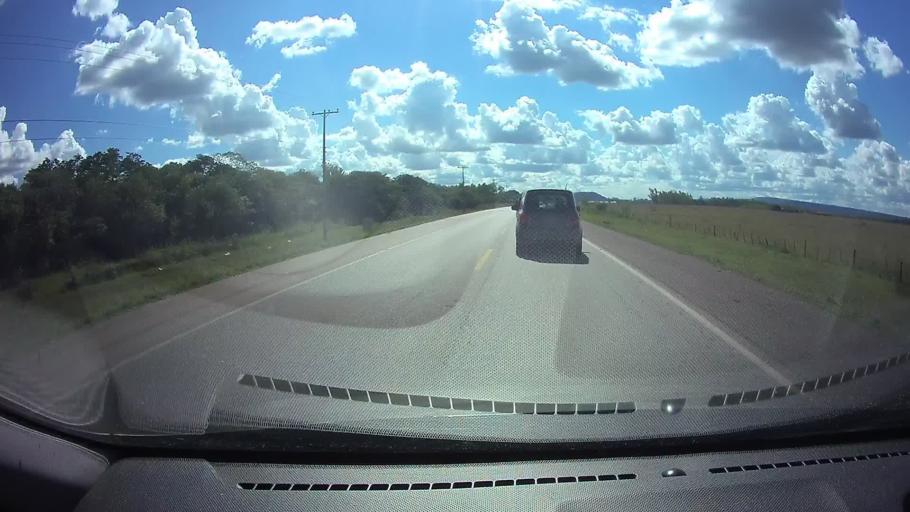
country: PY
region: Paraguari
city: La Colmena
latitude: -25.7489
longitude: -56.7964
